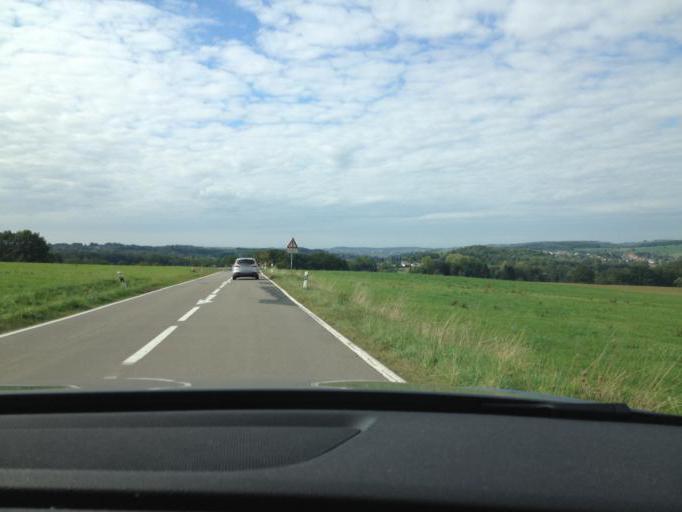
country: DE
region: Saarland
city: Mainzweiler
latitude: 49.4065
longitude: 7.1139
